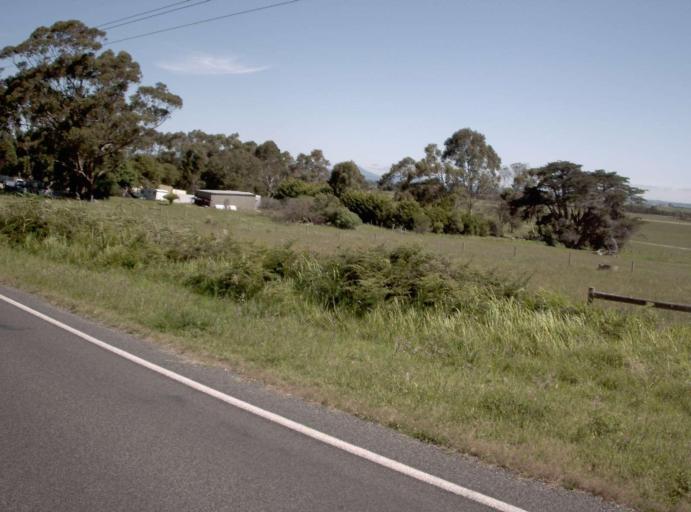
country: AU
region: Victoria
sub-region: Latrobe
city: Morwell
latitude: -38.6555
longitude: 146.3150
